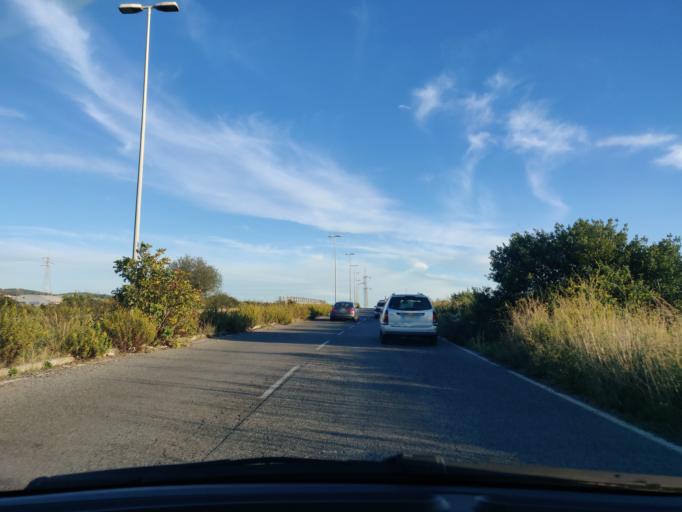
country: IT
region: Latium
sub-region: Citta metropolitana di Roma Capitale
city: Civitavecchia
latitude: 42.1095
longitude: 11.7853
